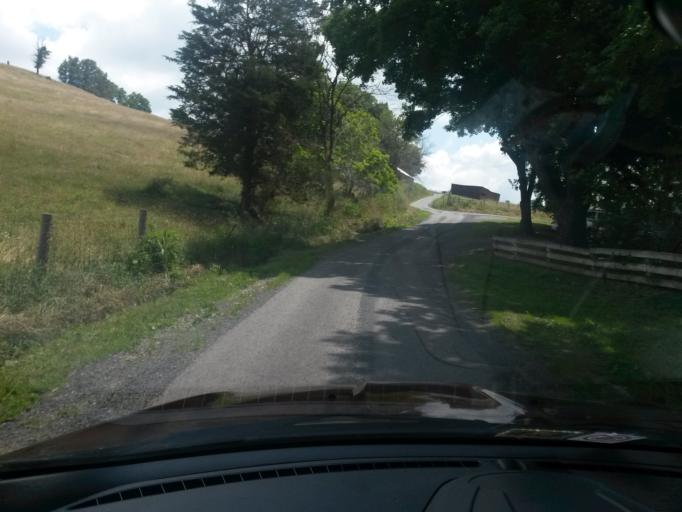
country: US
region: West Virginia
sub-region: Monroe County
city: Union
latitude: 37.5562
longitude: -80.5197
